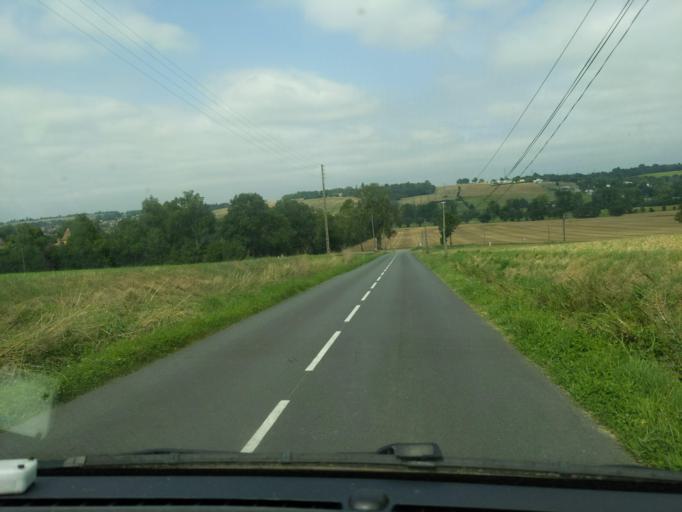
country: FR
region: Midi-Pyrenees
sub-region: Departement de la Haute-Garonne
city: Saint-Orens-de-Gameville
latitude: 43.5693
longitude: 1.5401
